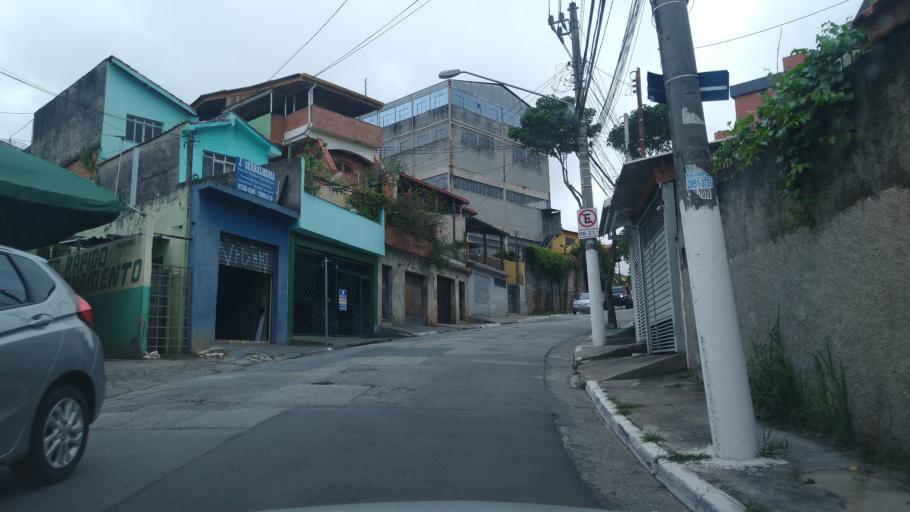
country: BR
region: Sao Paulo
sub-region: Sao Paulo
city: Sao Paulo
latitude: -23.4732
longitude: -46.6255
